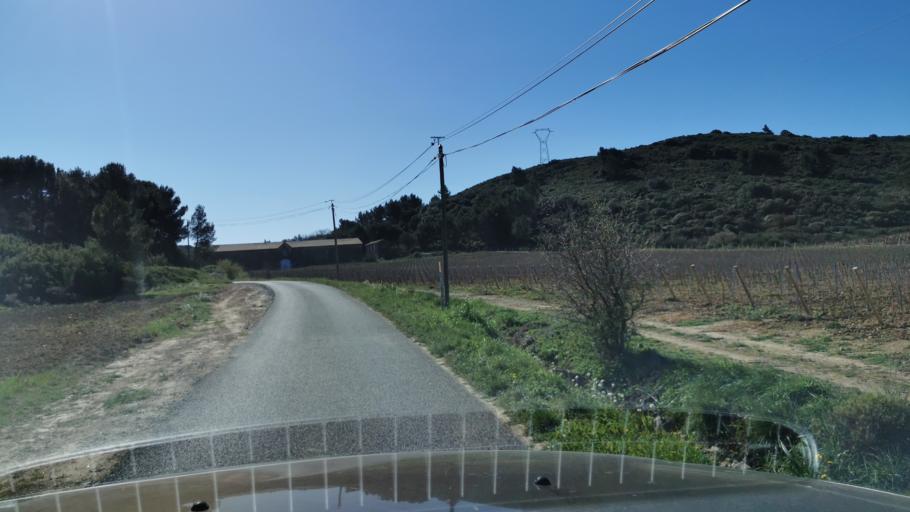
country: FR
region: Languedoc-Roussillon
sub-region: Departement de l'Aude
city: Narbonne
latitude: 43.1530
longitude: 2.9510
